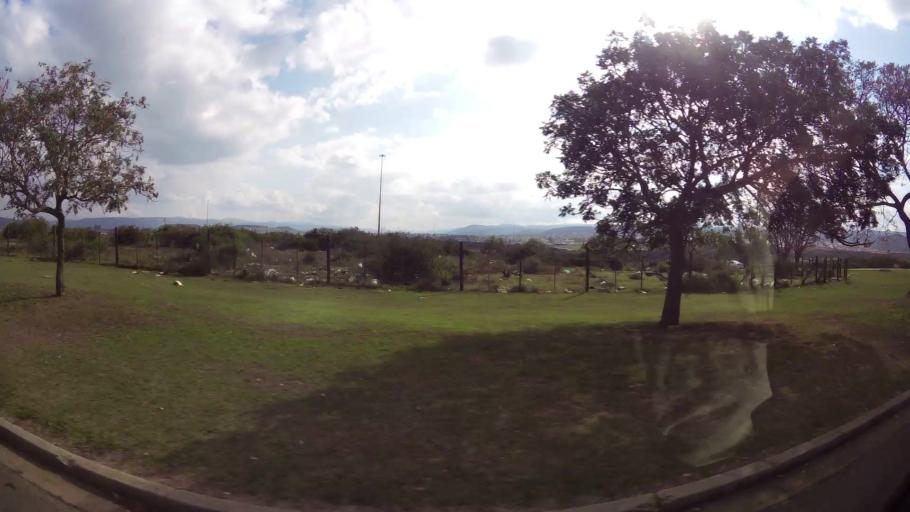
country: ZA
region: Eastern Cape
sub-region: Nelson Mandela Bay Metropolitan Municipality
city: Uitenhage
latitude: -33.7447
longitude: 25.4023
